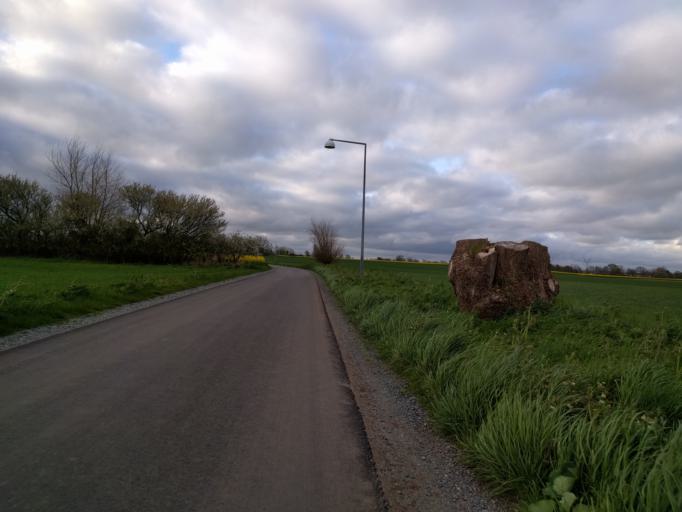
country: DK
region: South Denmark
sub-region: Odense Kommune
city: Bullerup
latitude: 55.4431
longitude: 10.4999
